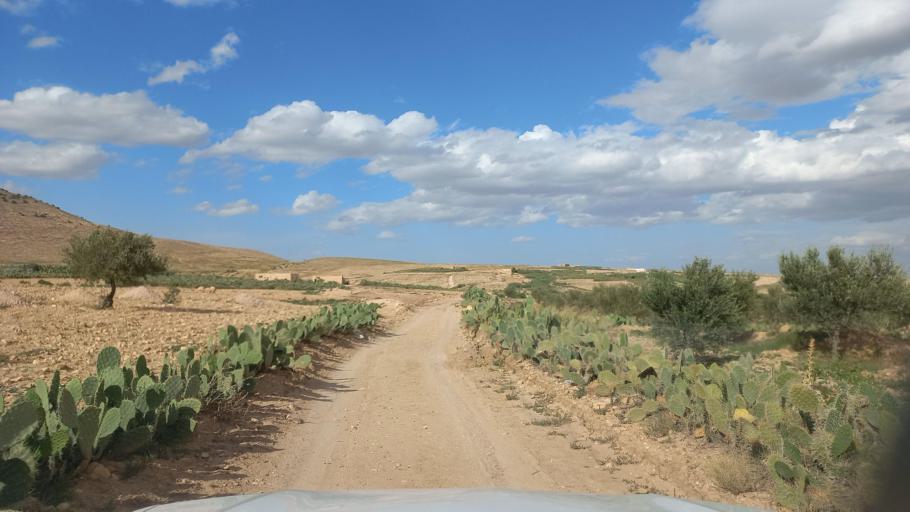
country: TN
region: Al Qasrayn
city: Sbiba
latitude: 35.4531
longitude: 9.0736
